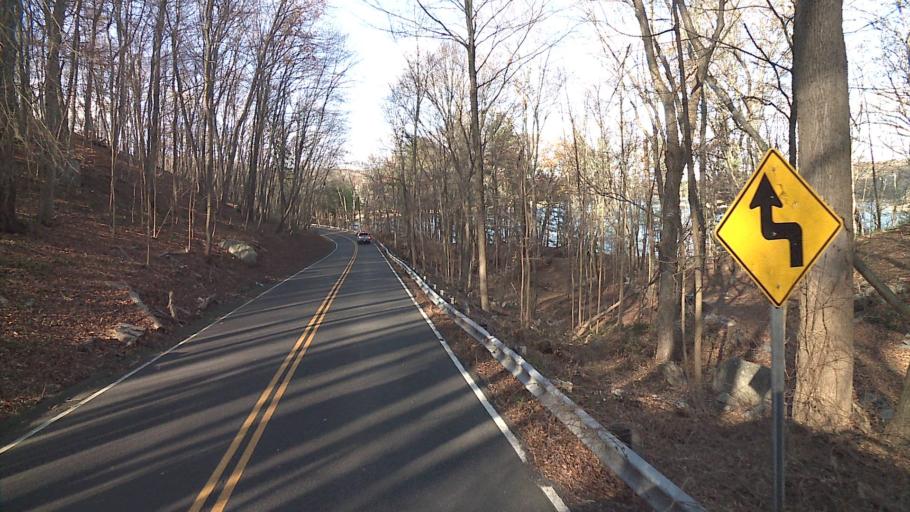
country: US
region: Connecticut
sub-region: Fairfield County
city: Georgetown
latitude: 41.2667
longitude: -73.3745
